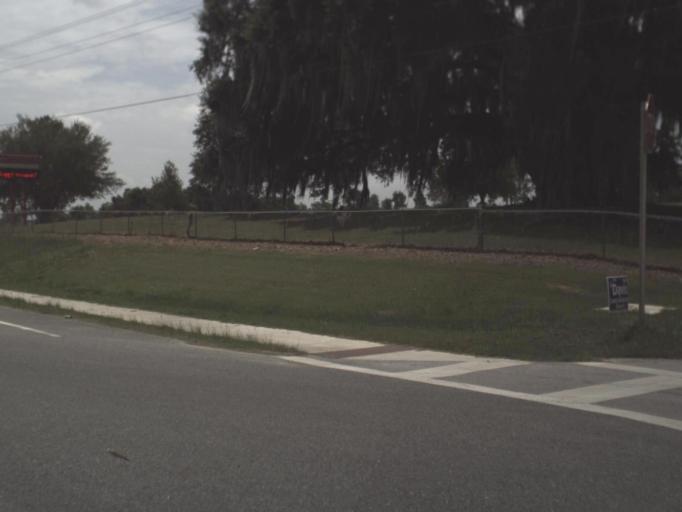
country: US
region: Florida
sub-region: Madison County
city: Madison
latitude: 30.4838
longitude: -83.4530
